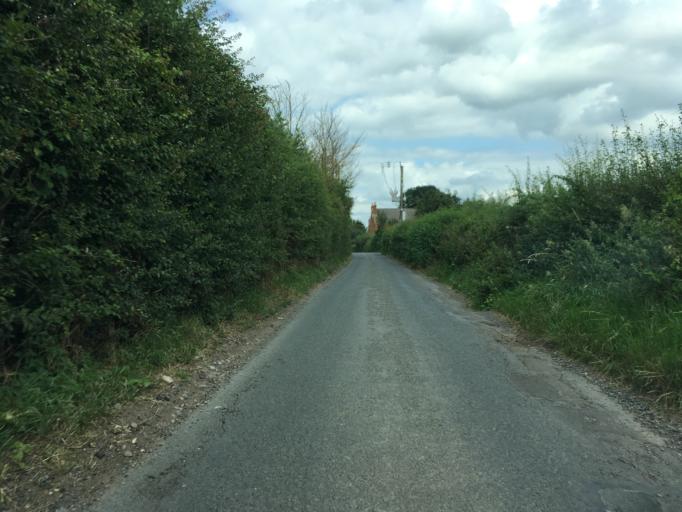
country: GB
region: England
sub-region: Gloucestershire
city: Gloucester
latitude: 51.9058
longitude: -2.2228
